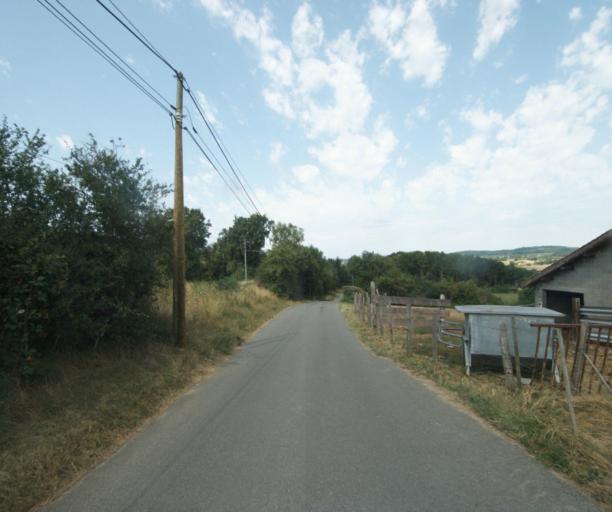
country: FR
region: Rhone-Alpes
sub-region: Departement du Rhone
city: Lentilly
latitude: 45.8474
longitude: 4.6557
